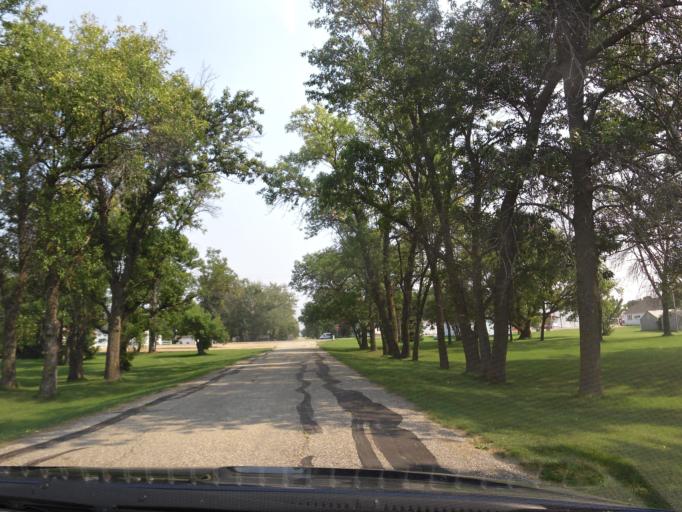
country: US
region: South Dakota
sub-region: Roberts County
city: Sisseton
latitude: 45.8578
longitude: -97.1053
